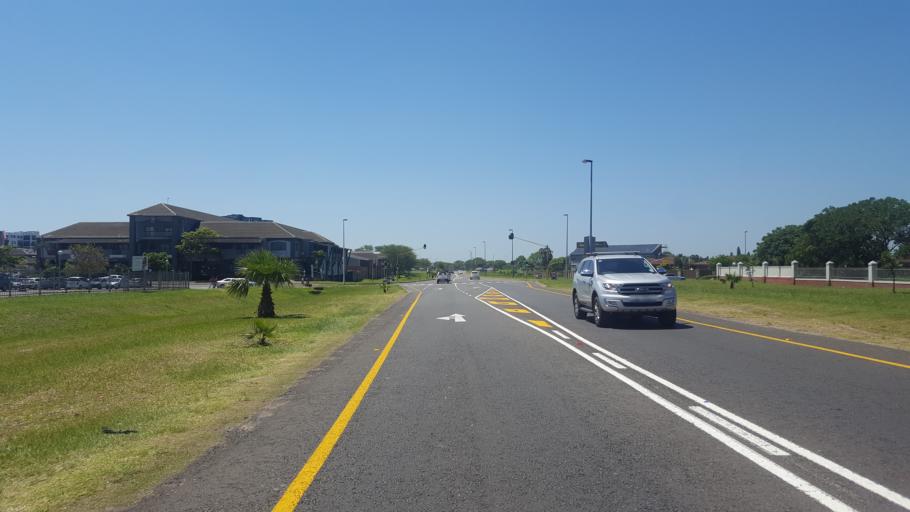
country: ZA
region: KwaZulu-Natal
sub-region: uThungulu District Municipality
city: Richards Bay
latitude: -28.7544
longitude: 32.0537
